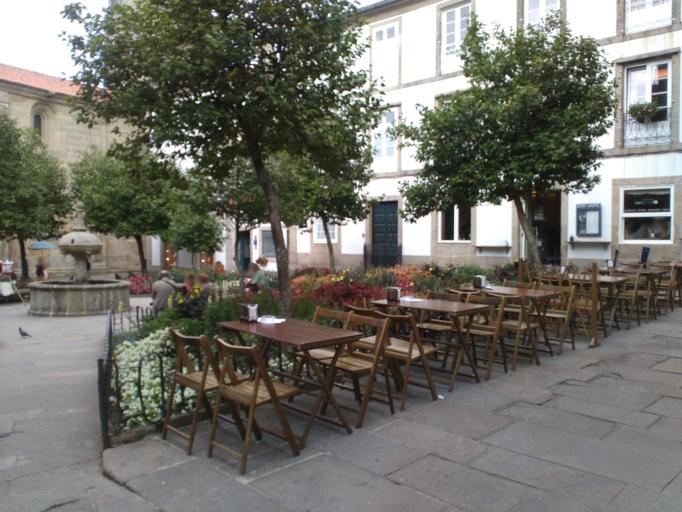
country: ES
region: Galicia
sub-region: Provincia da Coruna
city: Santiago de Compostela
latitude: 42.8793
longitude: -8.5448
